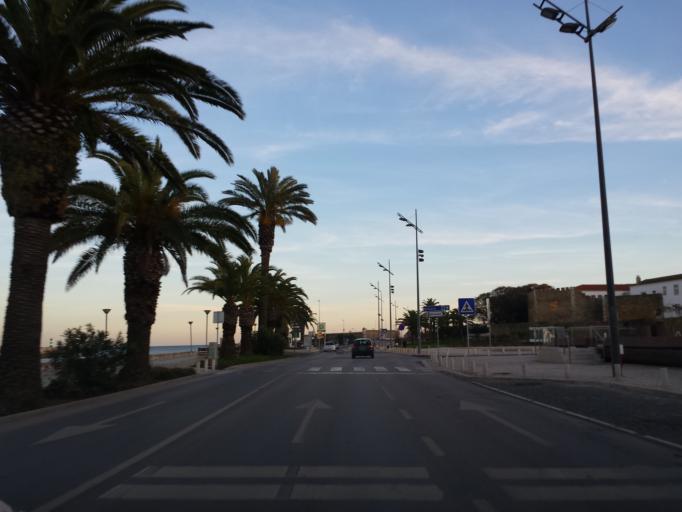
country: PT
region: Faro
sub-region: Lagos
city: Lagos
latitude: 37.1012
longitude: -8.6704
